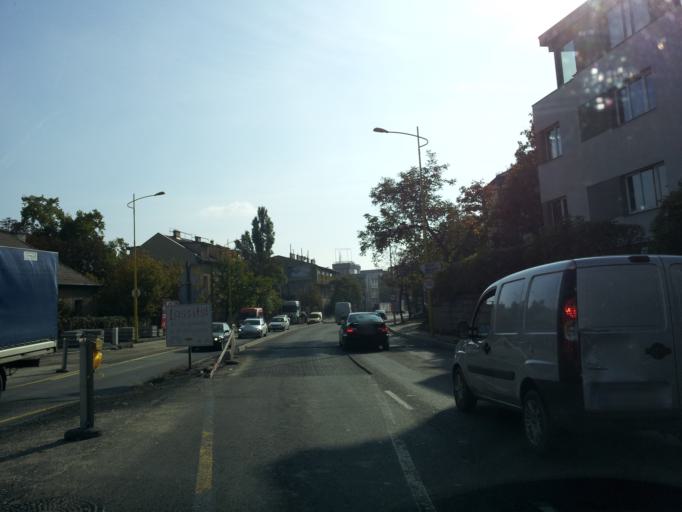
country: HU
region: Budapest
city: Budapest XI. keruelet
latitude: 47.4829
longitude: 19.0266
